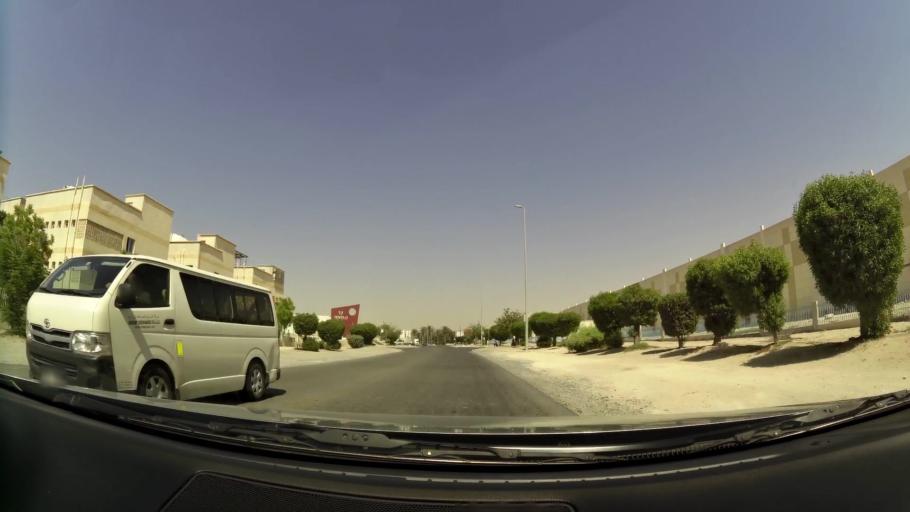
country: AE
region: Dubai
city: Dubai
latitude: 24.9706
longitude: 55.1698
